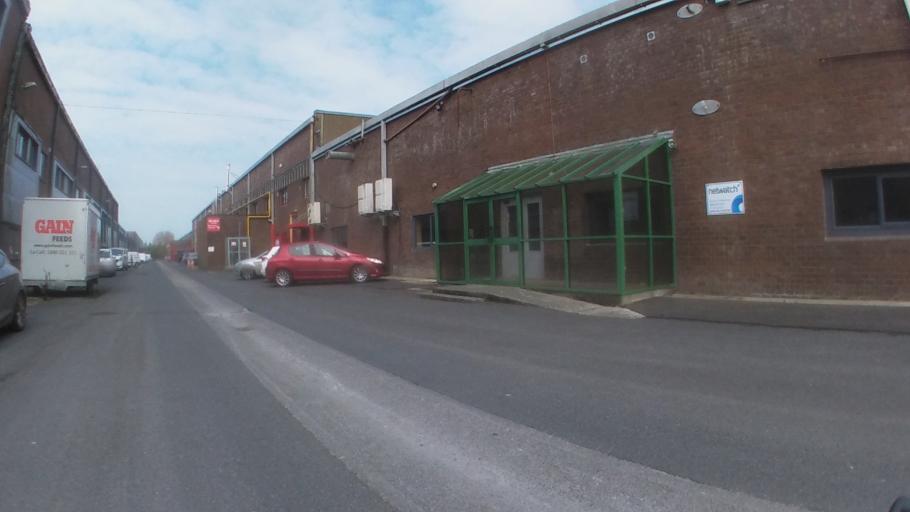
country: IE
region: Leinster
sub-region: Kilkenny
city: Kilkenny
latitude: 52.6442
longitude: -7.2110
